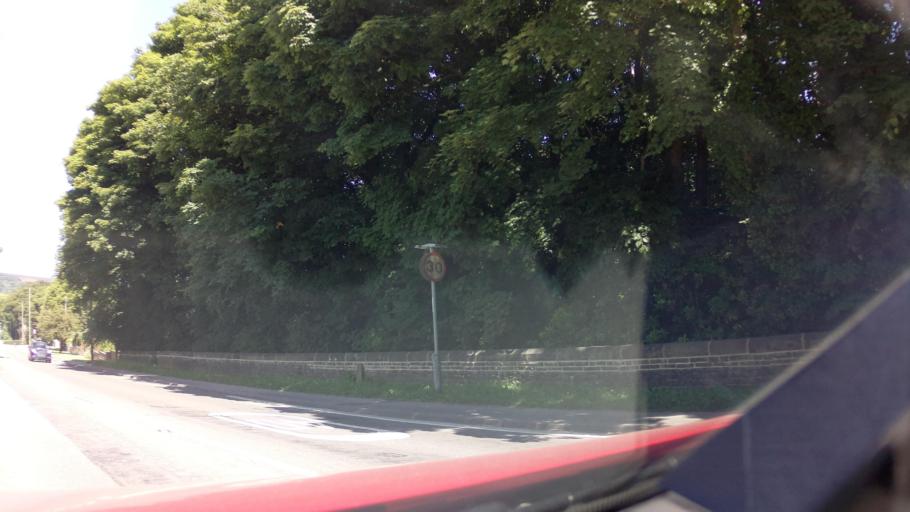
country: GB
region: England
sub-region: Derbyshire
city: Buxton
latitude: 53.2449
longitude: -1.9020
